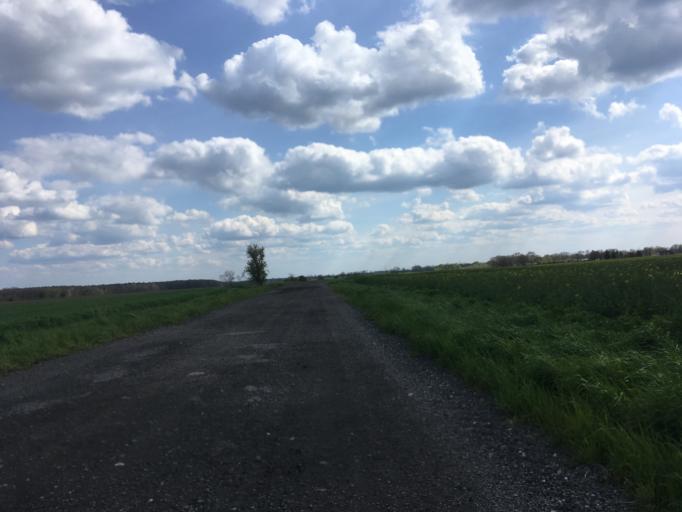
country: DE
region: Brandenburg
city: Werneuchen
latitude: 52.6058
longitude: 13.7005
